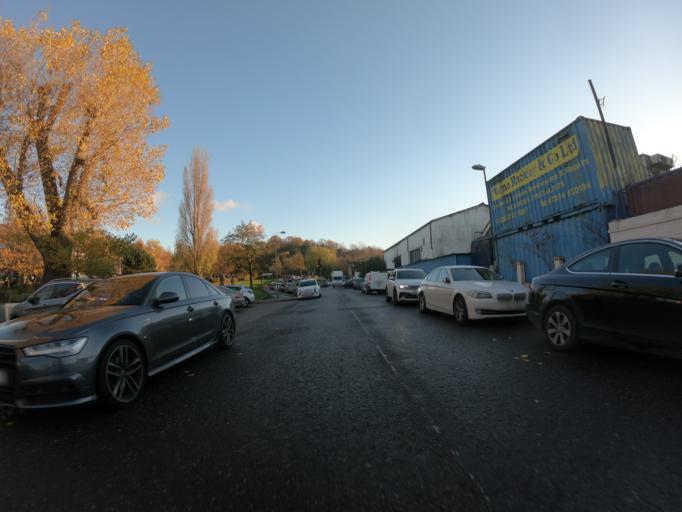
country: GB
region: England
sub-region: Greater London
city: Woolwich
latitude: 51.4920
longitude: 0.0395
